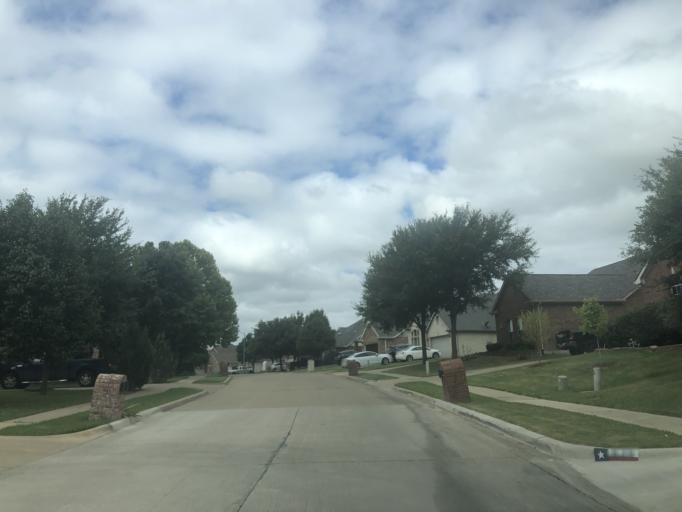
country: US
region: Texas
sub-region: Dallas County
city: Cedar Hill
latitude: 32.6533
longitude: -96.9975
